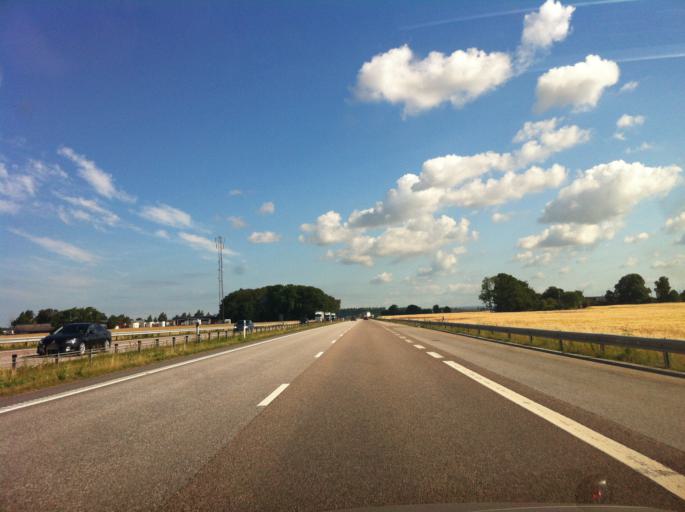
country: SE
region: Skane
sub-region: Angelholms Kommun
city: Strovelstorp
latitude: 56.1781
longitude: 12.8483
